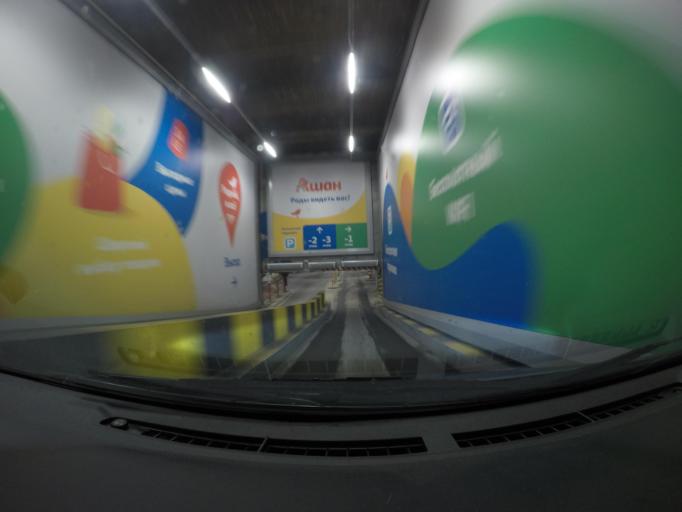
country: RU
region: Moscow
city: Sokol'niki
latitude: 55.7865
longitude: 37.6638
